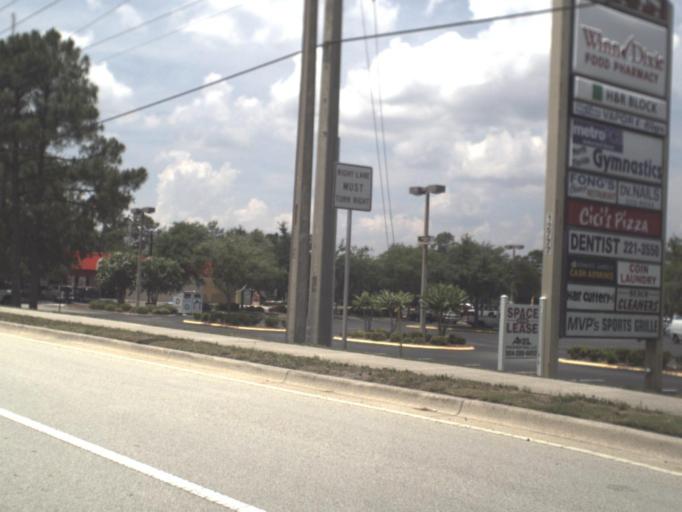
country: US
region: Florida
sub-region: Duval County
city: Atlantic Beach
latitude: 30.3193
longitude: -81.4706
